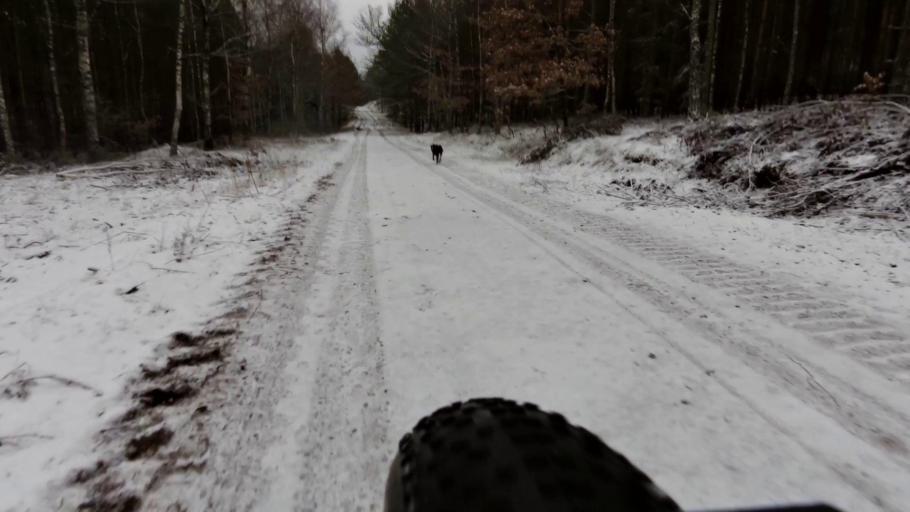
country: PL
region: West Pomeranian Voivodeship
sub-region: Powiat walecki
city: Miroslawiec
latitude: 53.2963
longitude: 16.0594
